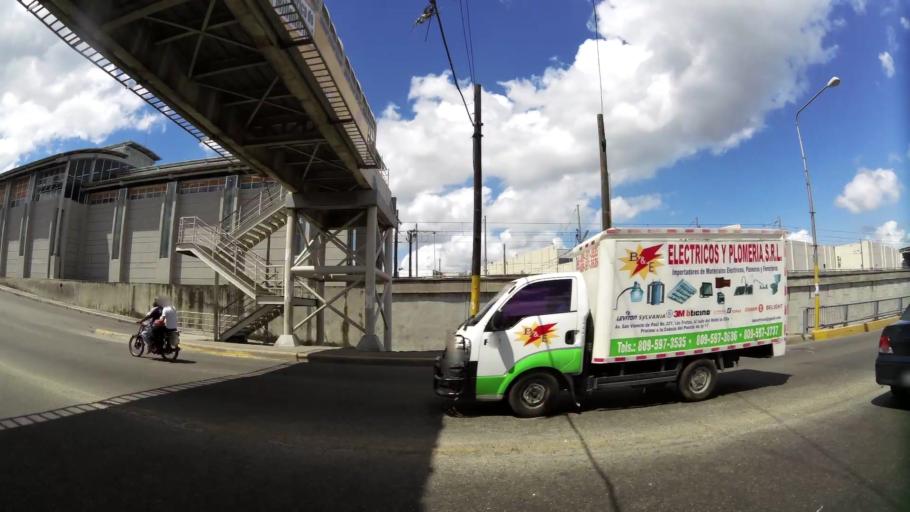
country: DO
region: Nacional
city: Ensanche Luperon
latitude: 18.5083
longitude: -69.9156
